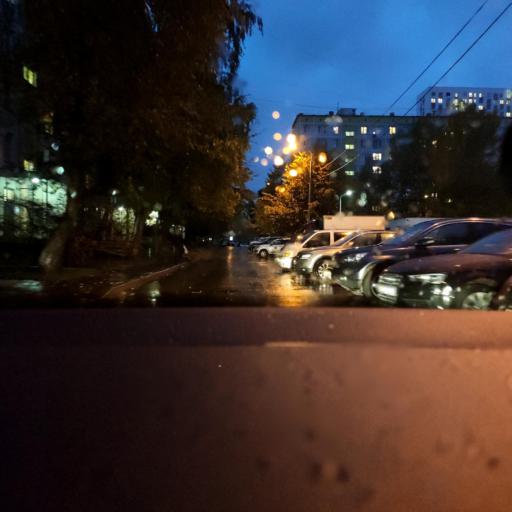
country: RU
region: Moskovskaya
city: Razvilka
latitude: 55.6019
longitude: 37.7389
